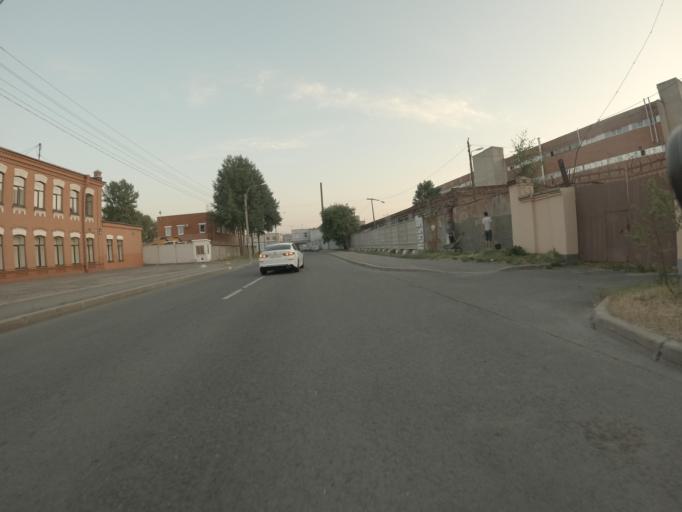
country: RU
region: St.-Petersburg
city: Centralniy
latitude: 59.8938
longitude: 30.3385
